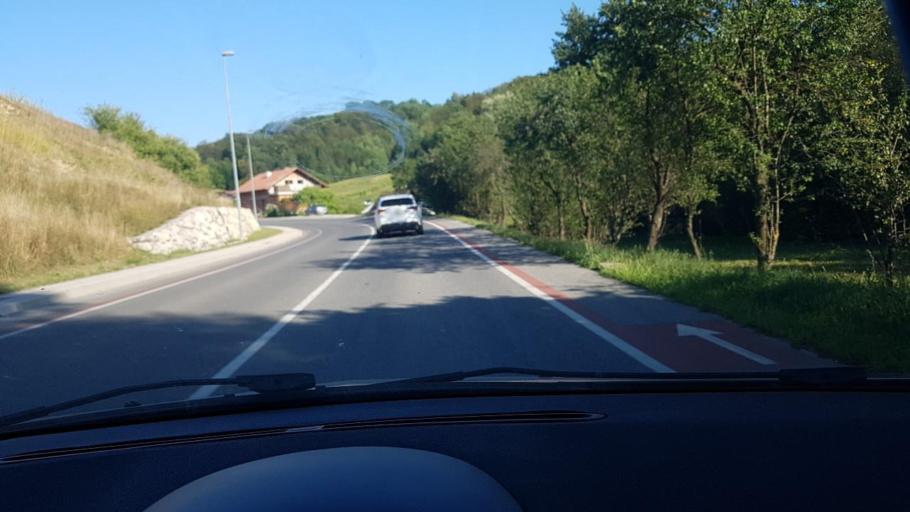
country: SI
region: Rogaska Slatina
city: Rogaska Slatina
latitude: 46.2393
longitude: 15.6128
